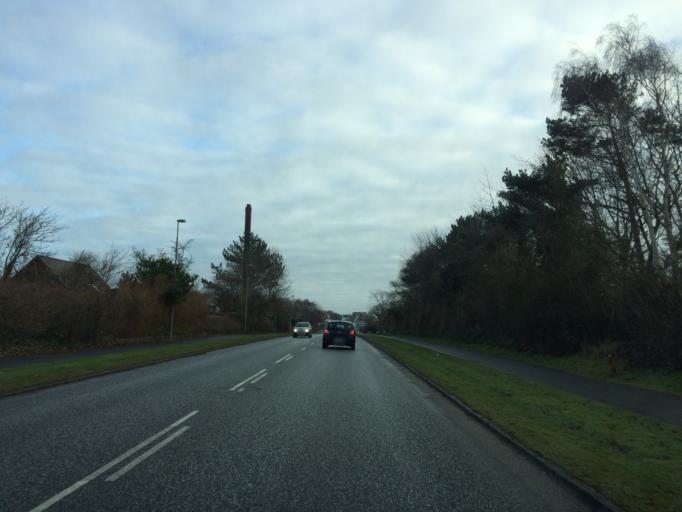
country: DK
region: Central Jutland
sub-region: Struer Kommune
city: Struer
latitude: 56.4889
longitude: 8.5765
